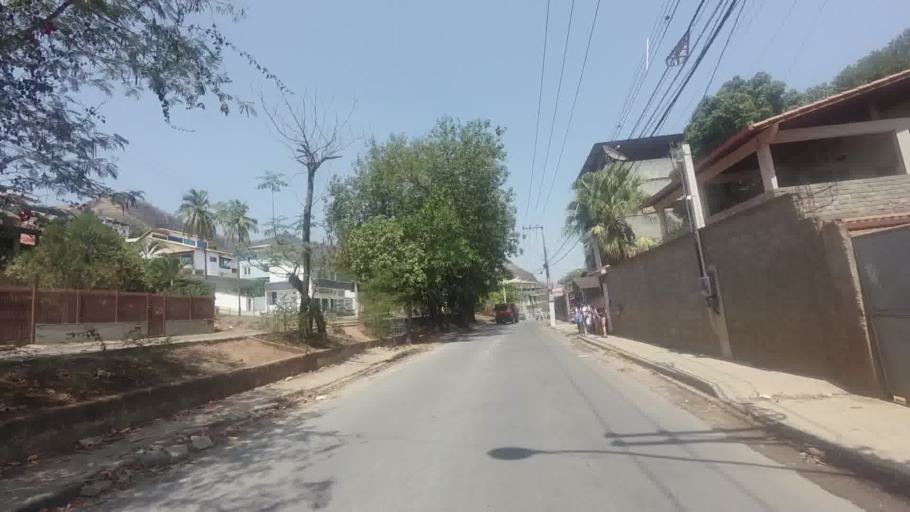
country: BR
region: Espirito Santo
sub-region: Cachoeiro De Itapemirim
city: Cachoeiro de Itapemirim
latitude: -20.8521
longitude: -41.1492
